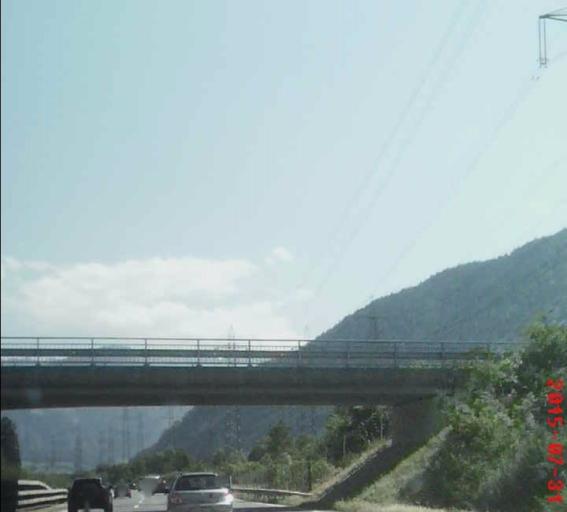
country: CH
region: Grisons
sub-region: Landquart District
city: Maienfeld
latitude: 47.0025
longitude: 9.5202
